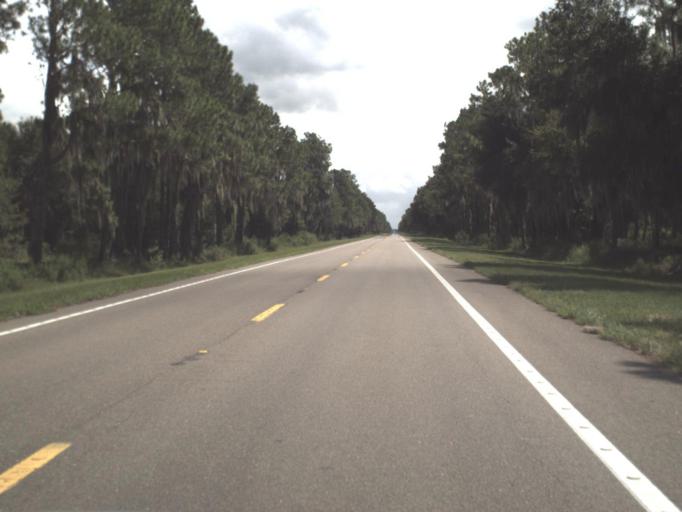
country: US
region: Florida
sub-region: Polk County
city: Mulberry
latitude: 27.7047
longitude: -82.0423
